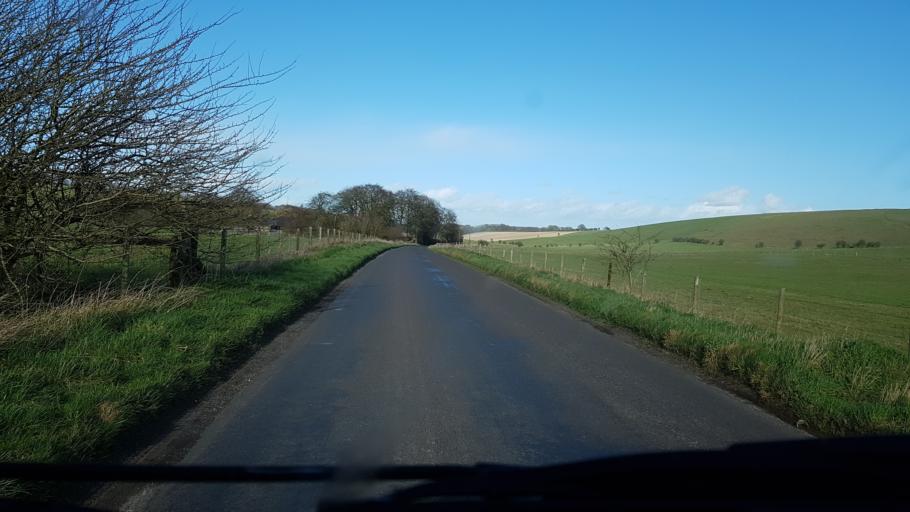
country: GB
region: England
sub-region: Wiltshire
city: Woodborough
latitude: 51.3737
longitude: -1.8347
